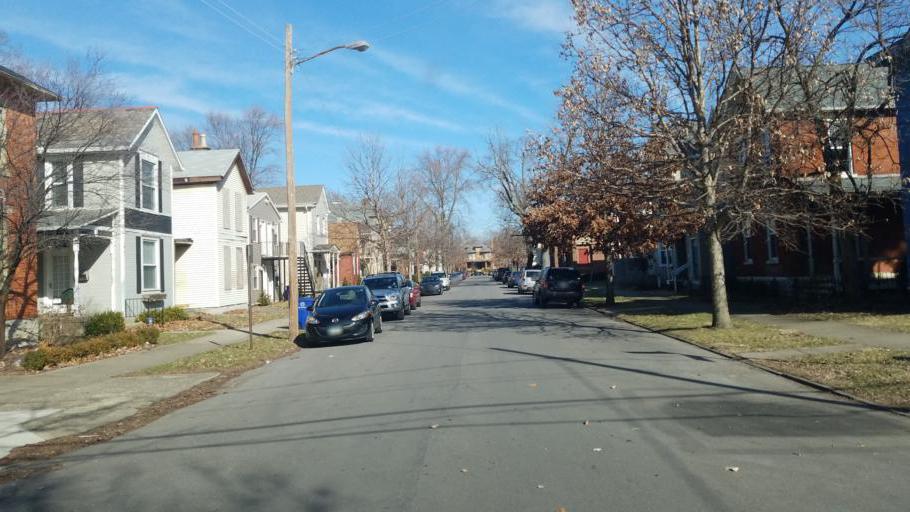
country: US
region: Ohio
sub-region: Franklin County
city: Columbus
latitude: 39.9586
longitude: -82.9785
